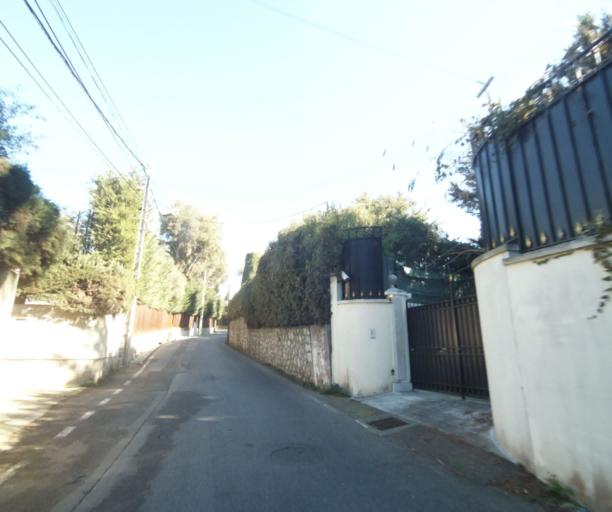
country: FR
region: Provence-Alpes-Cote d'Azur
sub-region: Departement des Alpes-Maritimes
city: Antibes
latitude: 43.5597
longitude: 7.1263
